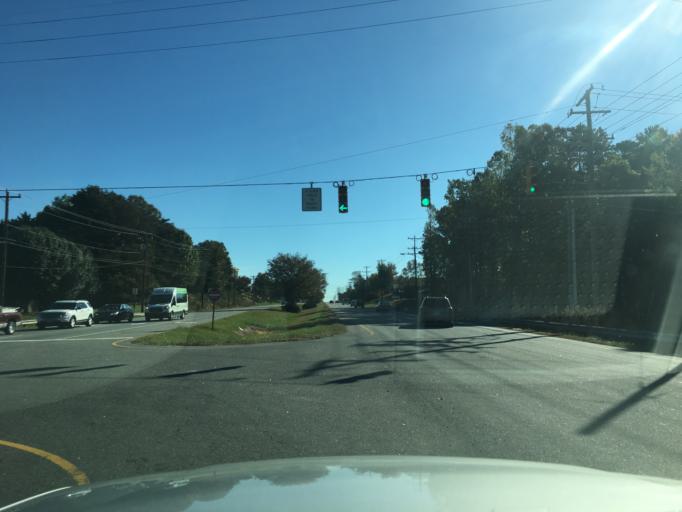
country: US
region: North Carolina
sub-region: Catawba County
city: Hickory
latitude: 35.7289
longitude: -81.3092
